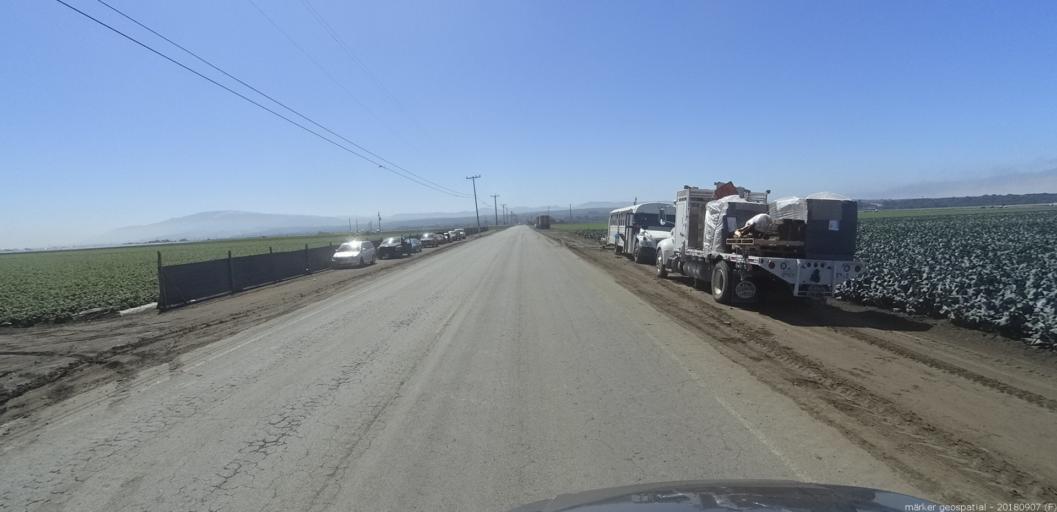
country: US
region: California
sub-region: Monterey County
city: Boronda
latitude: 36.6916
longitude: -121.7350
